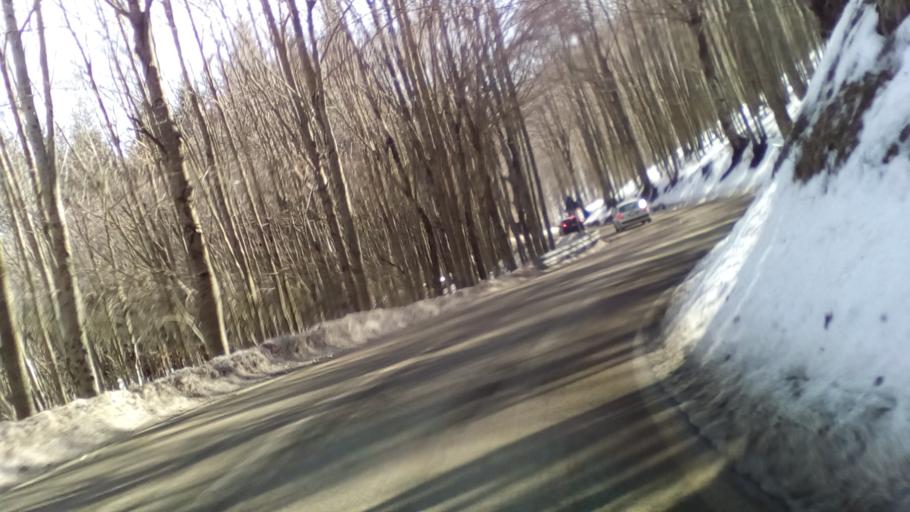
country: IT
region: Tuscany
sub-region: Provincia di Lucca
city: Fosciandora
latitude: 44.1973
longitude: 10.5073
